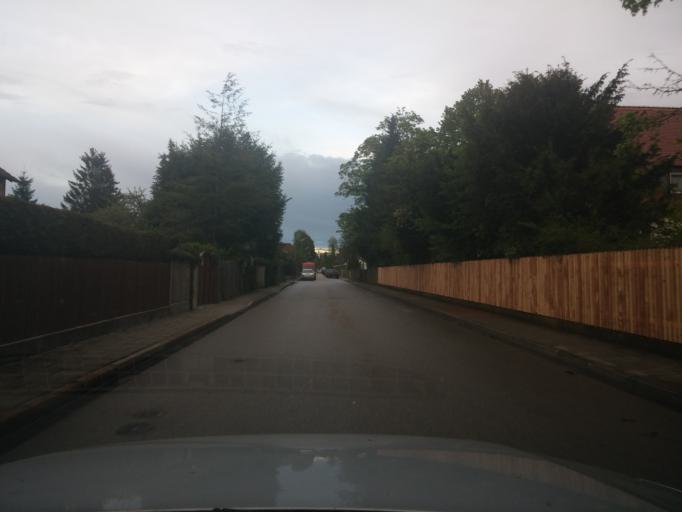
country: DE
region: Bavaria
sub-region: Upper Bavaria
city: Haar
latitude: 48.1061
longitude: 11.7414
